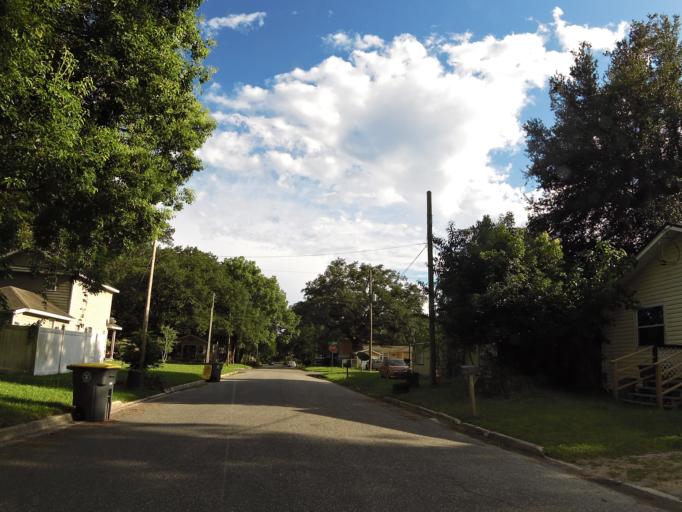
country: US
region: Florida
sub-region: Duval County
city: Jacksonville
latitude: 30.3197
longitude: -81.7075
